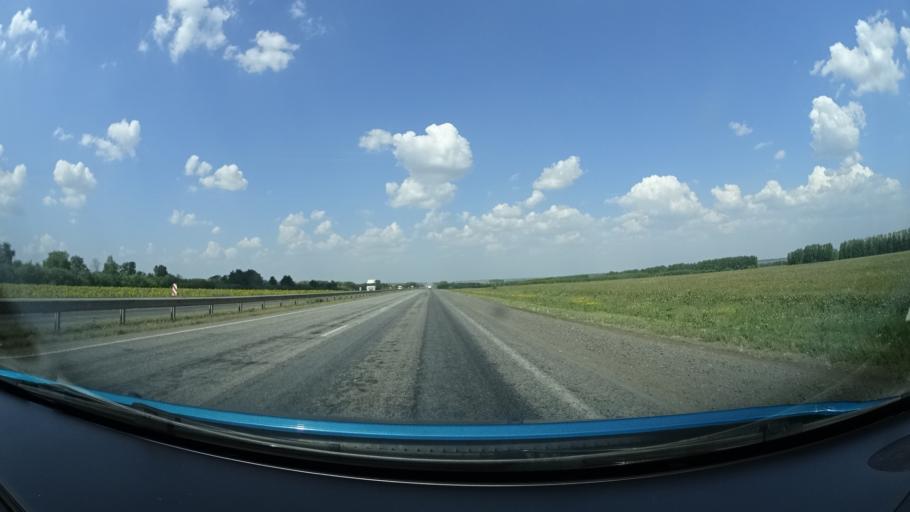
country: RU
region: Bashkortostan
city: Dmitriyevka
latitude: 54.7078
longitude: 55.2289
